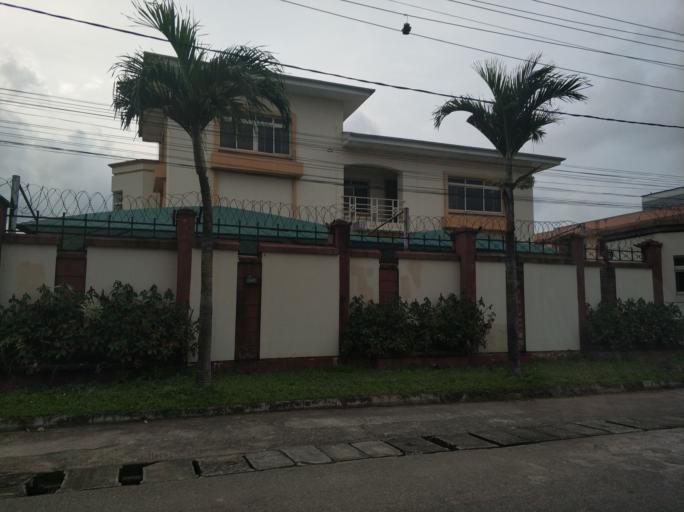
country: NG
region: Lagos
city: Ikoyi
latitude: 6.4619
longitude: 3.4396
